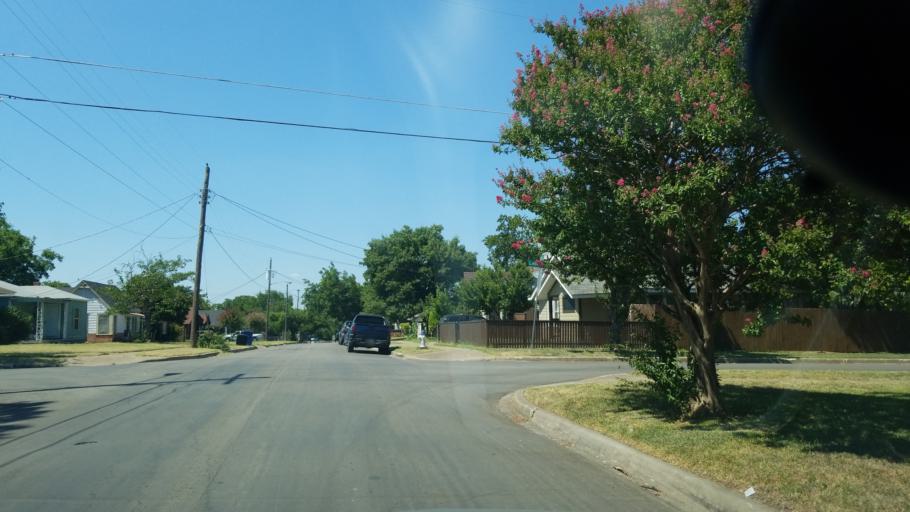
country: US
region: Texas
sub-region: Dallas County
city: Cockrell Hill
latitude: 32.7323
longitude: -96.8469
